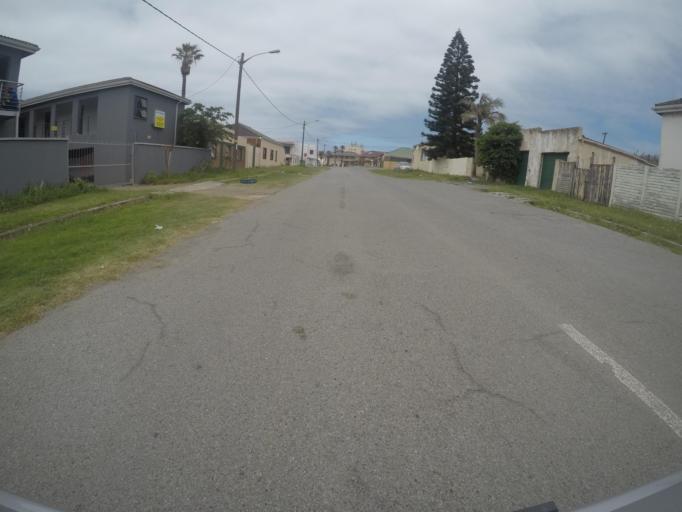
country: ZA
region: Eastern Cape
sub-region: Buffalo City Metropolitan Municipality
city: East London
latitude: -33.0133
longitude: 27.9184
